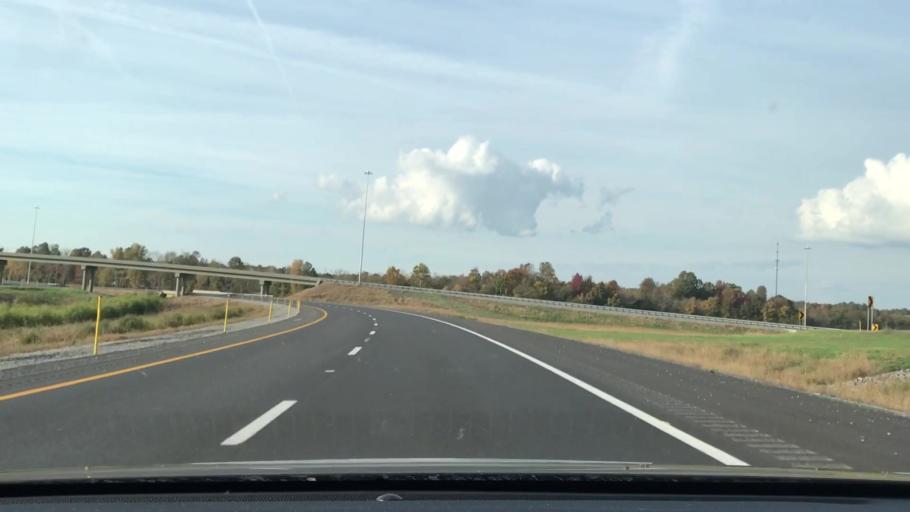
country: US
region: Kentucky
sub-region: Marshall County
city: Calvert City
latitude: 36.9894
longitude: -88.3441
